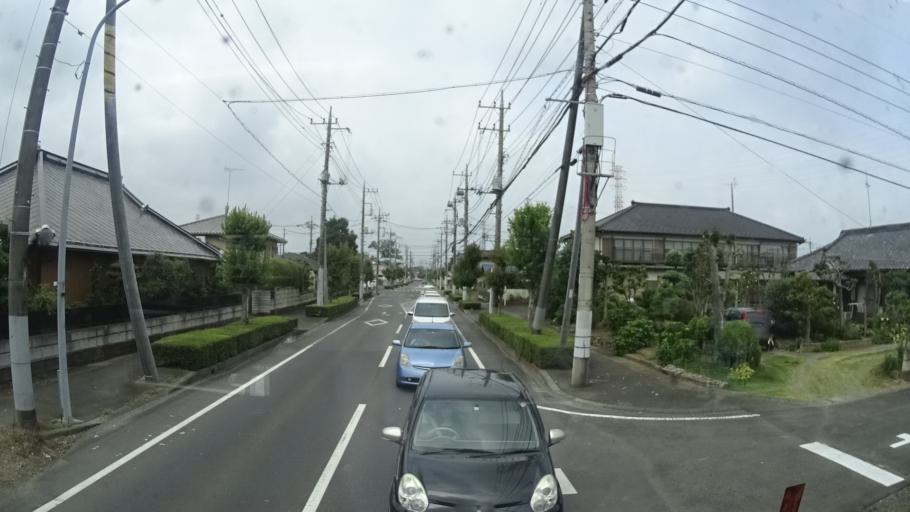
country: JP
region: Ibaraki
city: Shimodate
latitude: 36.3073
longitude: 139.9712
